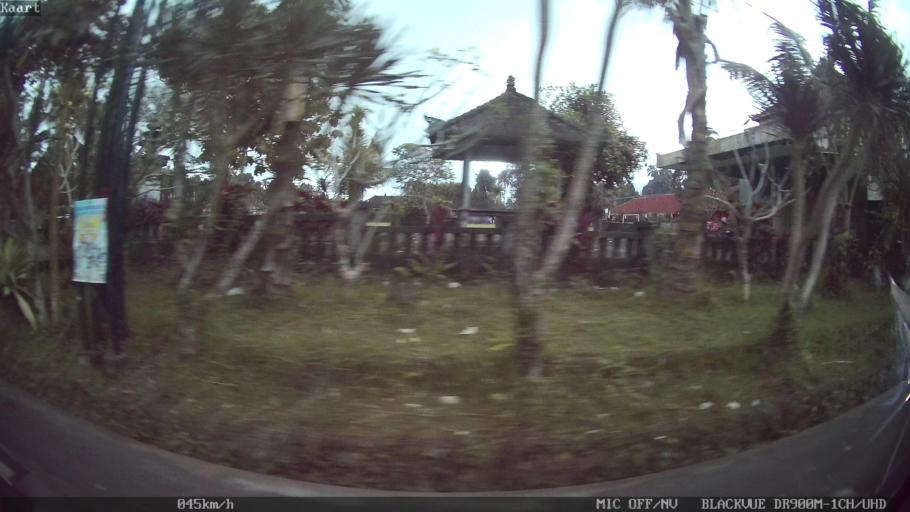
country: ID
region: Bali
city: Banjar Kubu
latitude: -8.4285
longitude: 115.4291
